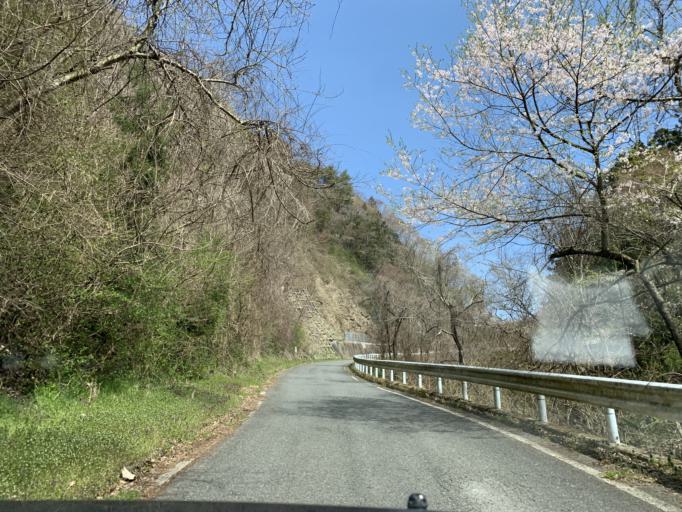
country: JP
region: Iwate
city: Ichinoseki
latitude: 38.7980
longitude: 141.2580
